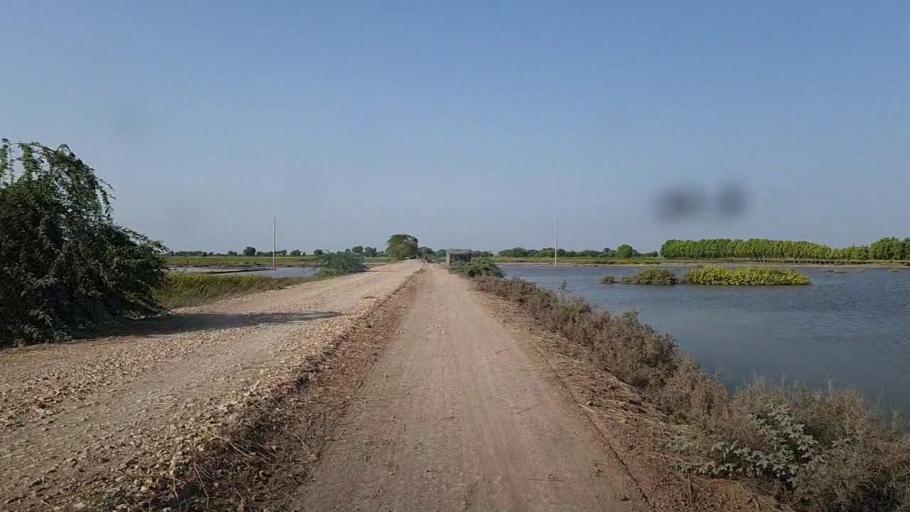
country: PK
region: Sindh
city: Bulri
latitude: 24.7757
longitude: 68.4336
